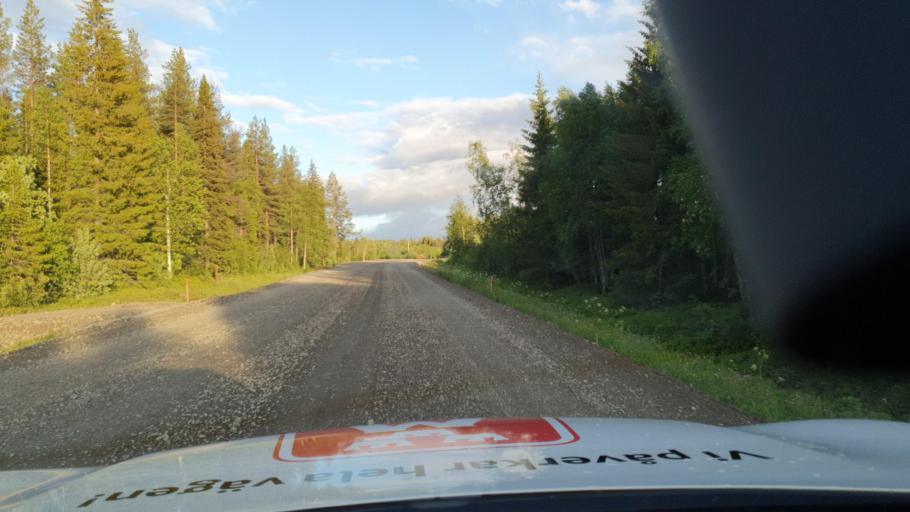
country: SE
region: Vaesterbotten
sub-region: Lycksele Kommun
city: Soderfors
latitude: 64.6599
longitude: 17.8398
